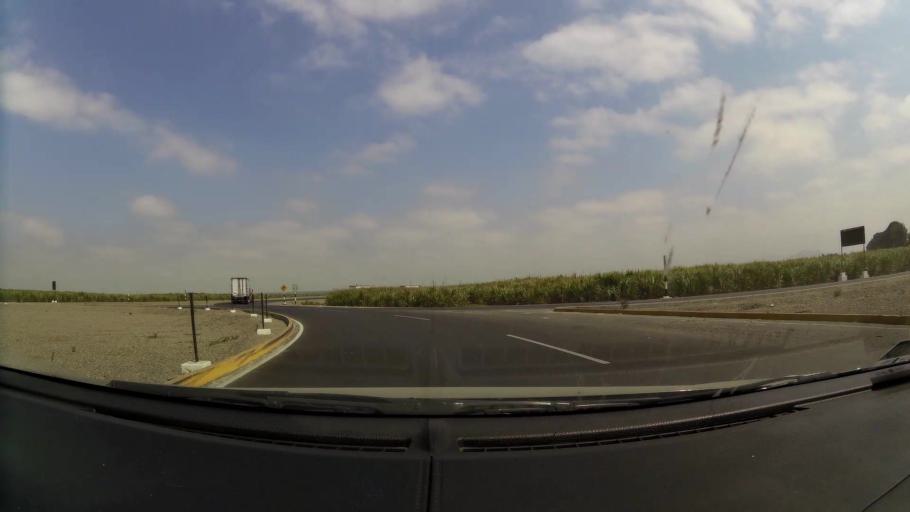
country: PE
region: La Libertad
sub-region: Ascope
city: Chicama
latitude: -7.8611
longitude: -79.1408
